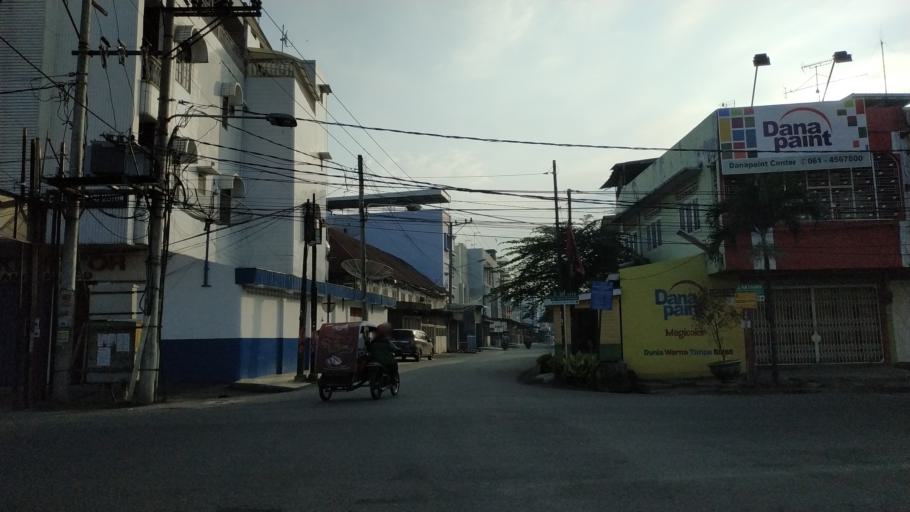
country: ID
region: North Sumatra
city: Medan
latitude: 3.5951
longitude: 98.6877
